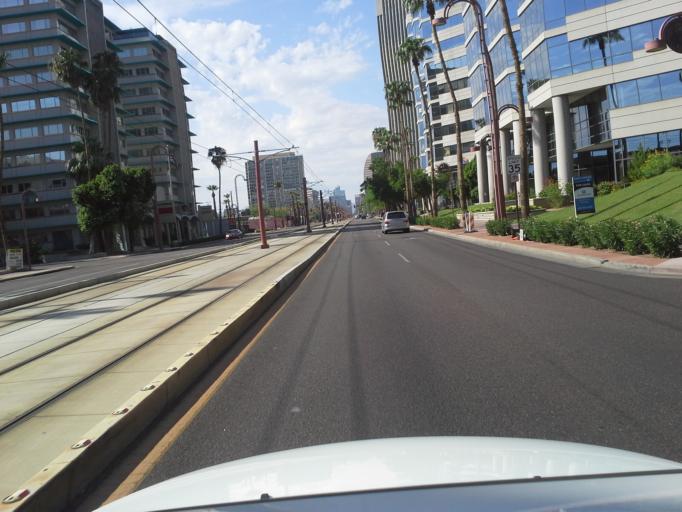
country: US
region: Arizona
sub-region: Maricopa County
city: Phoenix
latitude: 33.4793
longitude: -112.0739
